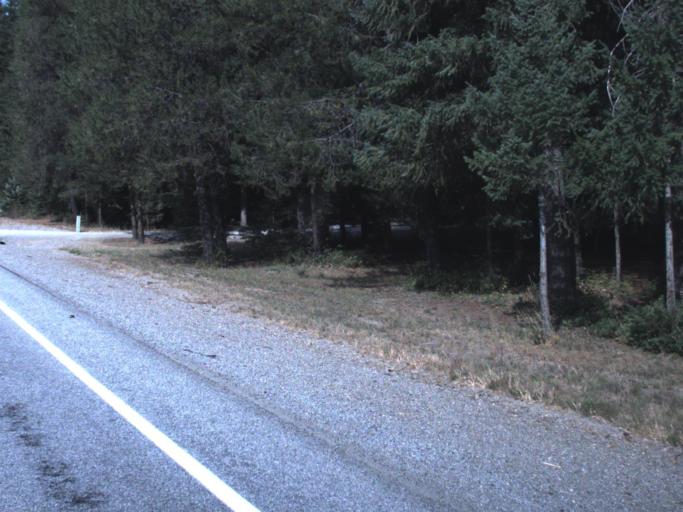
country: US
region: Washington
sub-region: Pend Oreille County
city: Newport
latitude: 48.2763
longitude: -117.2846
